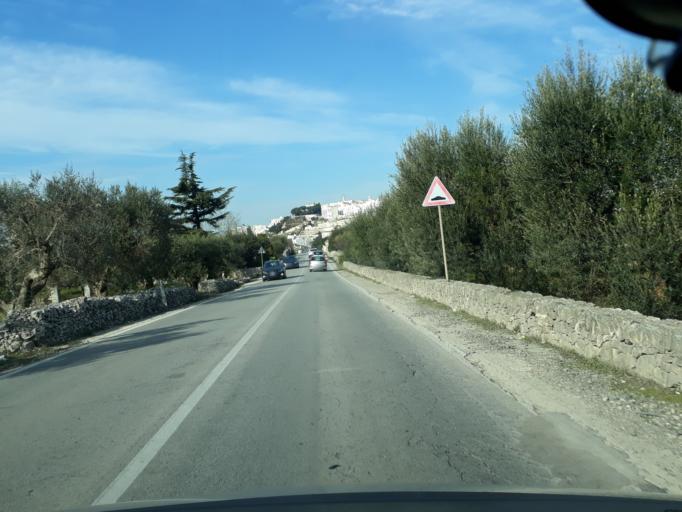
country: IT
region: Apulia
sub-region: Provincia di Bari
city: Locorotondo
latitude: 40.7435
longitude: 17.3318
